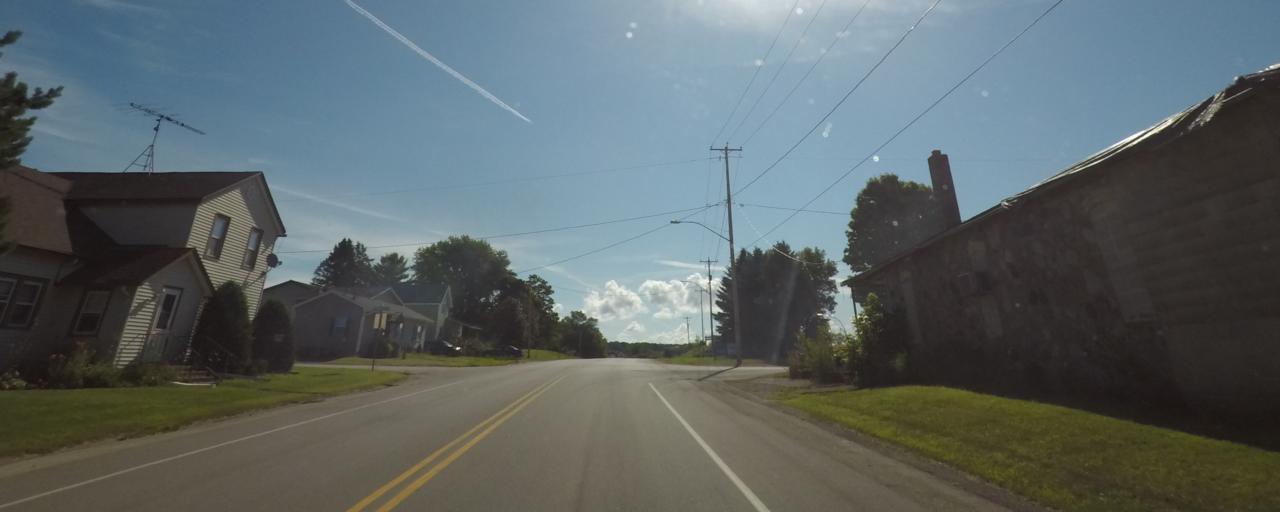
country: US
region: Wisconsin
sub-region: Jefferson County
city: Ixonia
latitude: 43.0760
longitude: -88.6728
